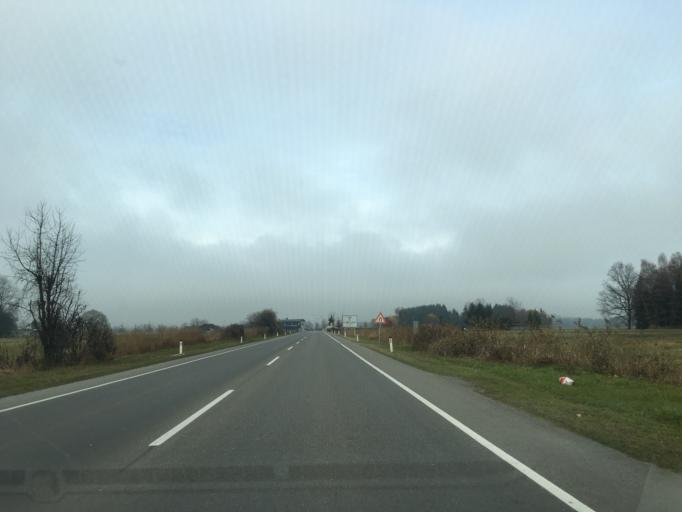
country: CH
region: Saint Gallen
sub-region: Wahlkreis Rheintal
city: Diepoldsau
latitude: 47.3949
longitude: 9.6805
